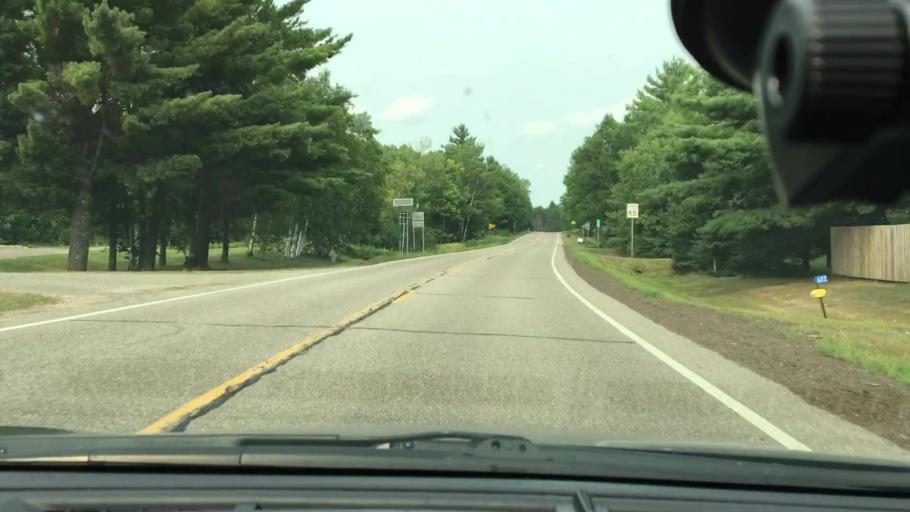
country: US
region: Minnesota
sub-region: Crow Wing County
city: Cross Lake
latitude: 46.8255
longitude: -93.9477
